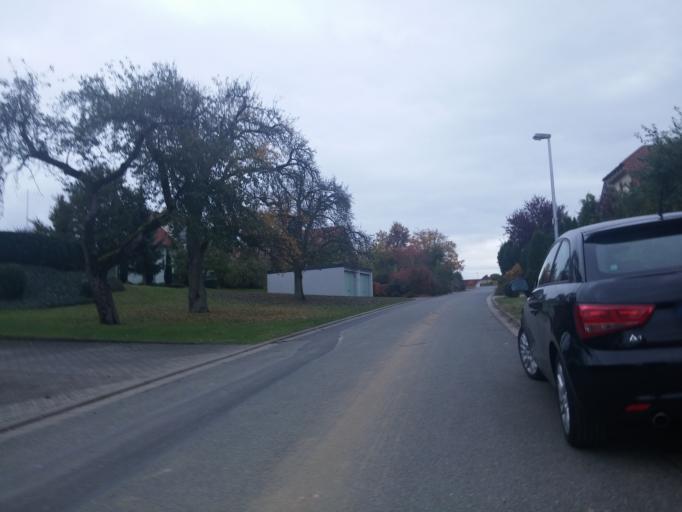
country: DE
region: Bavaria
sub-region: Upper Franconia
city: Grossheirath
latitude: 50.1742
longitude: 10.9507
